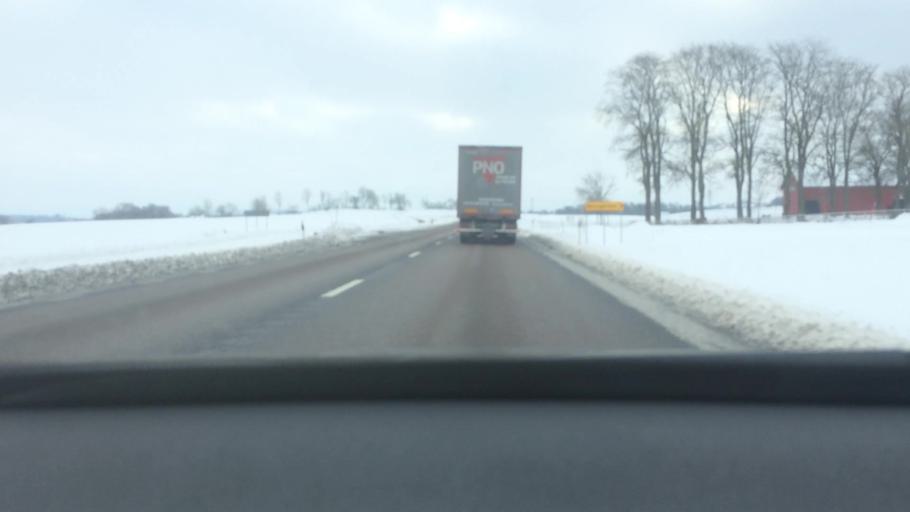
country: SE
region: Vaestra Goetaland
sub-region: Falkopings Kommun
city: Falkoeping
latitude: 58.2038
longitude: 13.5605
